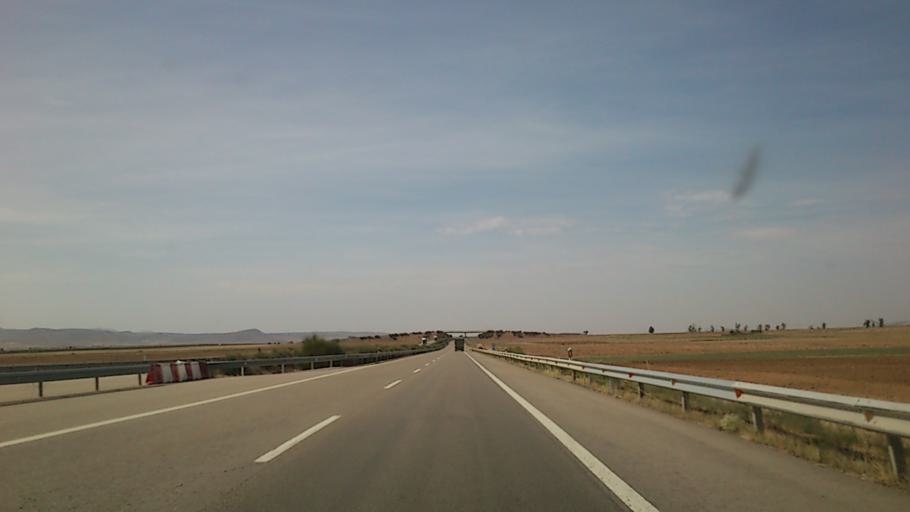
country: ES
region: Aragon
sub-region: Provincia de Teruel
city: Villarquemado
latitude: 40.5296
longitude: -1.2604
